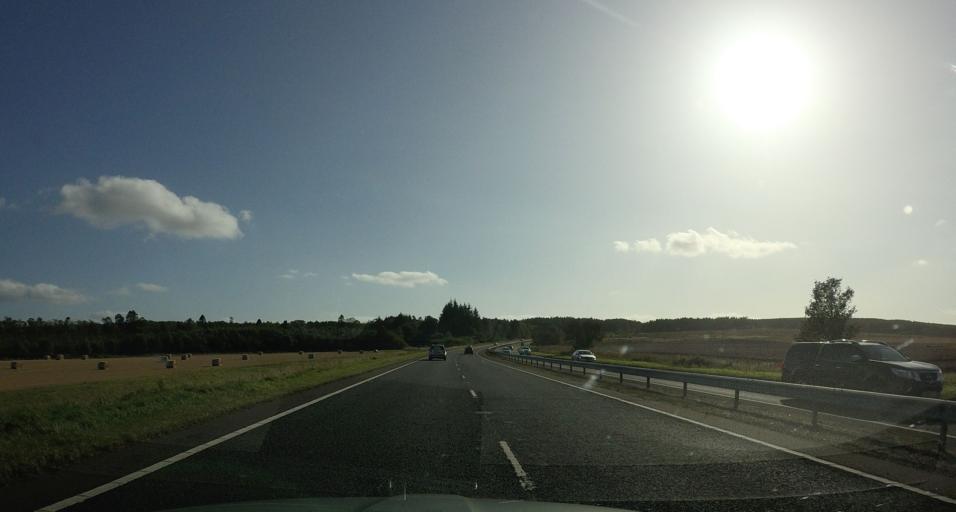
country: GB
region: Scotland
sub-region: Angus
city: Forfar
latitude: 56.5605
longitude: -2.9222
